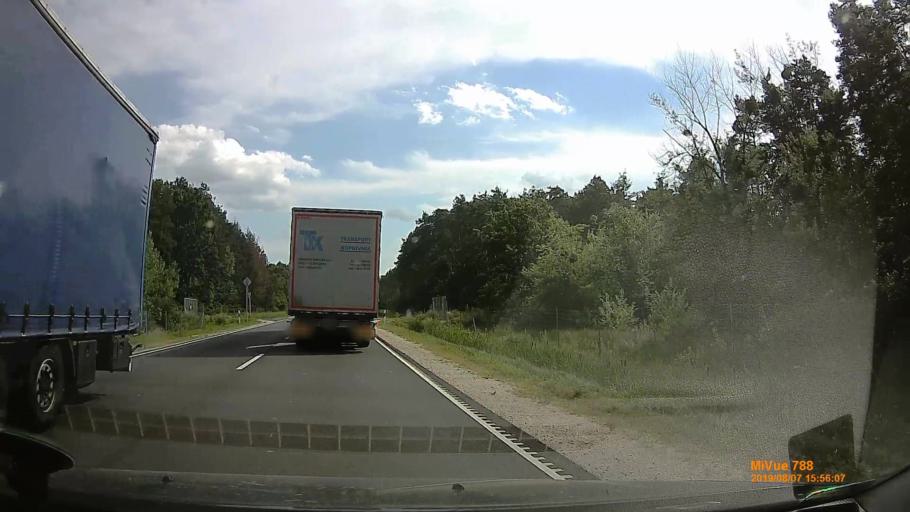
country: HU
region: Vas
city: Kormend
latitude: 47.0651
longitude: 16.6167
